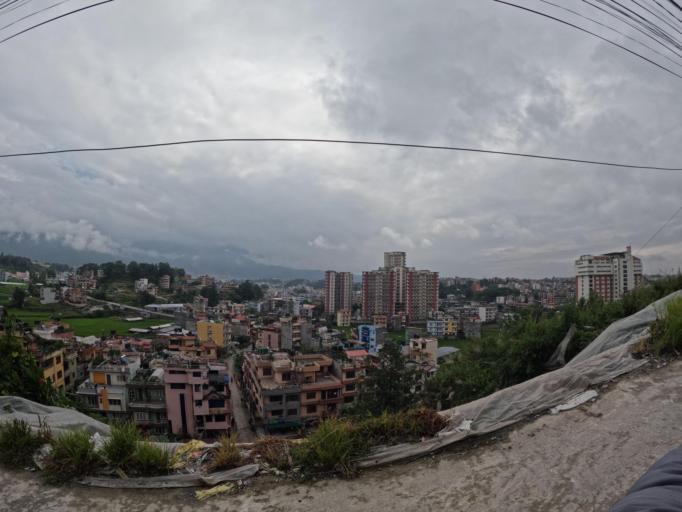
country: NP
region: Central Region
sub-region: Bagmati Zone
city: Kathmandu
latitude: 27.7548
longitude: 85.3229
